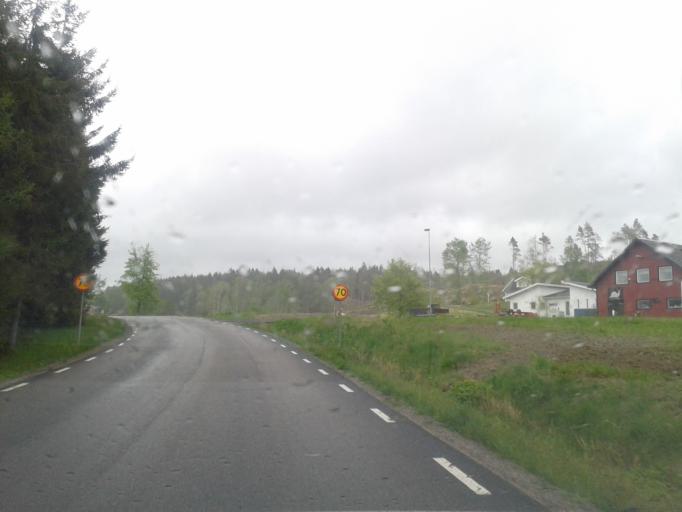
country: SE
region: Vaestra Goetaland
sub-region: Kungalvs Kommun
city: Kungalv
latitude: 57.9044
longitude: 11.9353
